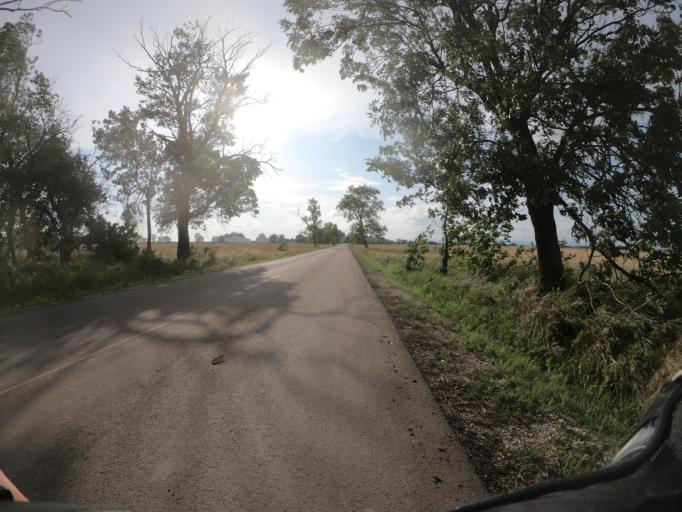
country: HU
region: Borsod-Abauj-Zemplen
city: Emod
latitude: 47.8278
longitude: 20.8070
